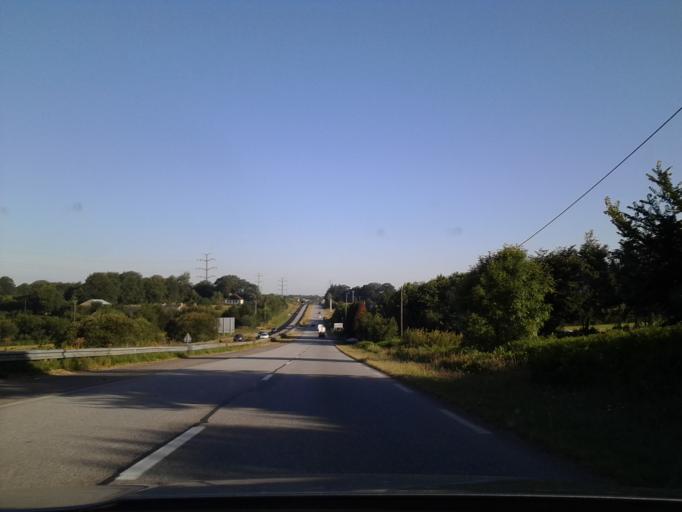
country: FR
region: Lower Normandy
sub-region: Departement de la Manche
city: La Glacerie
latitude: 49.5780
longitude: -1.5822
